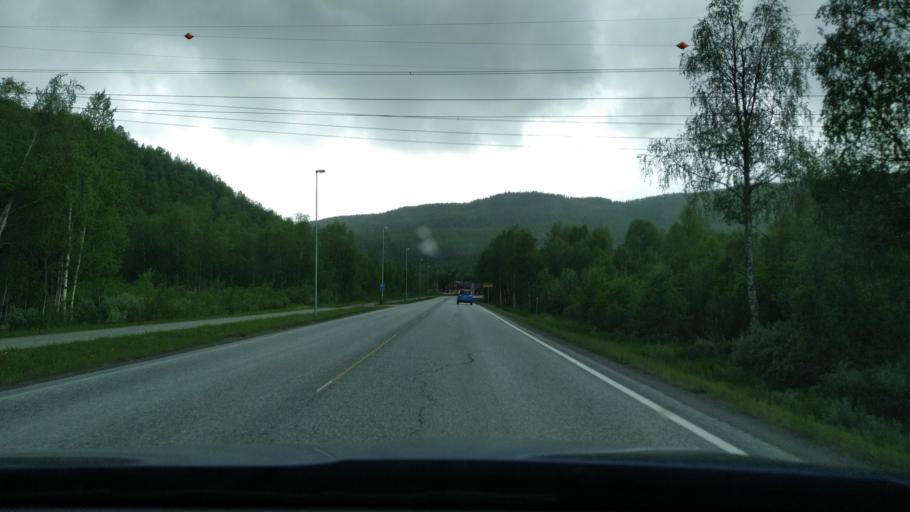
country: NO
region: Troms
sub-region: Malselv
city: Moen
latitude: 69.0090
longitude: 18.5031
